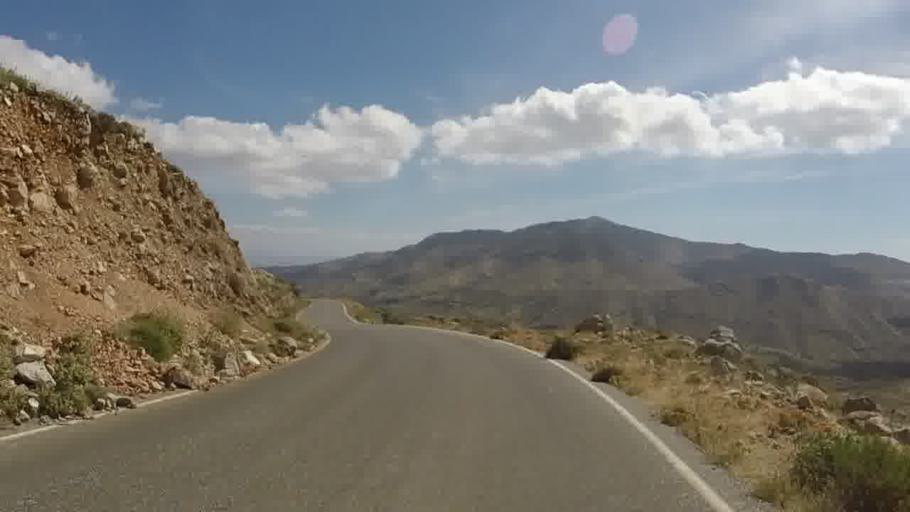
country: GR
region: Crete
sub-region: Nomos Rethymnis
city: Agia Galini
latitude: 35.1564
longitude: 24.6171
